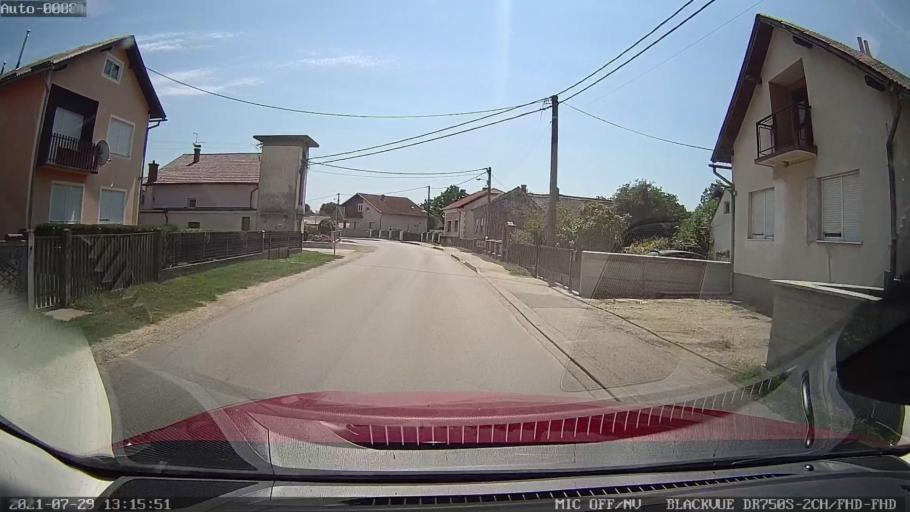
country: HR
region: Medimurska
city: Kursanec
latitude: 46.2818
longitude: 16.3902
